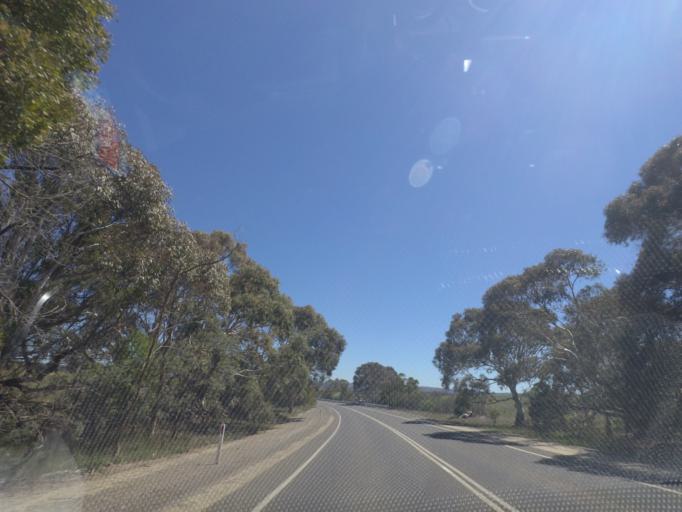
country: AU
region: Victoria
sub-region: Hume
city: Sunbury
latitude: -37.2878
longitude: 144.7877
